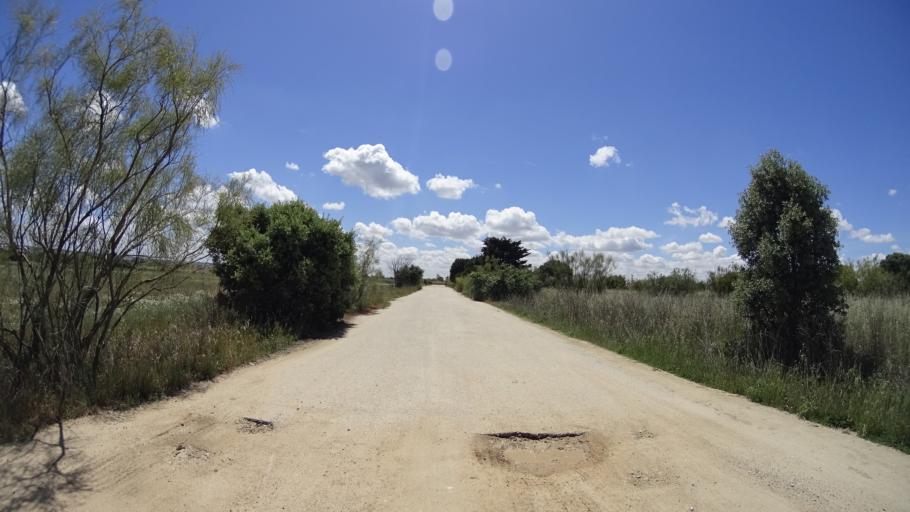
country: ES
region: Madrid
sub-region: Provincia de Madrid
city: Villanueva del Pardillo
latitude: 40.4860
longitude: -3.9861
